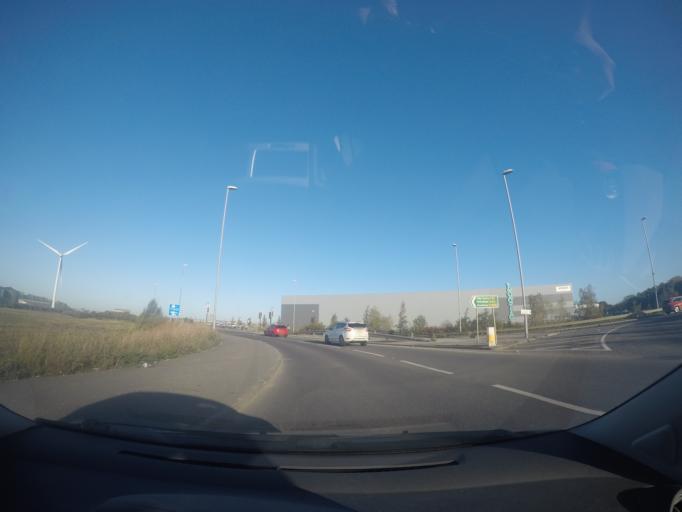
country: GB
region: England
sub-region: City and Borough of Leeds
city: Lofthouse
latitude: 53.7804
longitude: -1.4819
